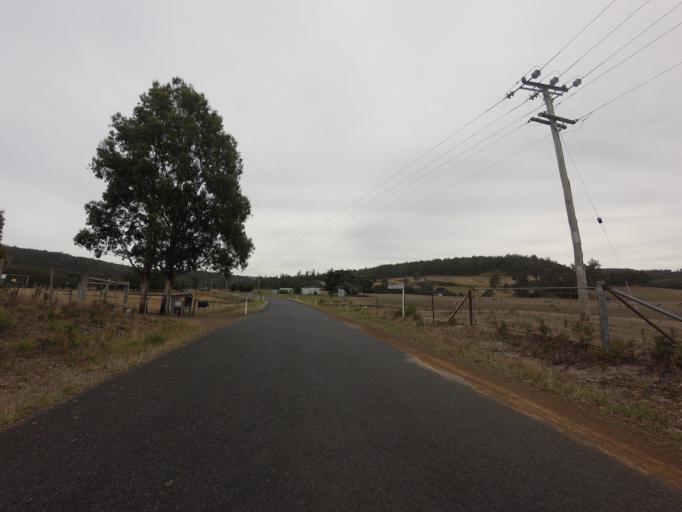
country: AU
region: Tasmania
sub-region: Sorell
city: Sorell
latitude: -42.5633
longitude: 147.5716
